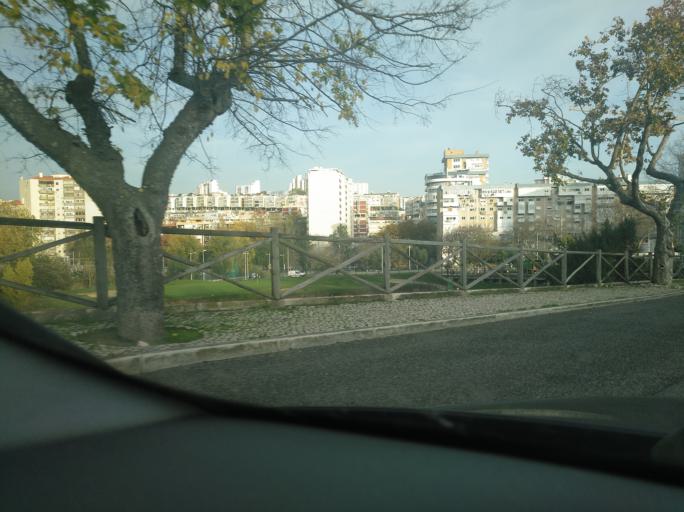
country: PT
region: Lisbon
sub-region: Odivelas
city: Olival do Basto
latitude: 38.7790
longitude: -9.1684
